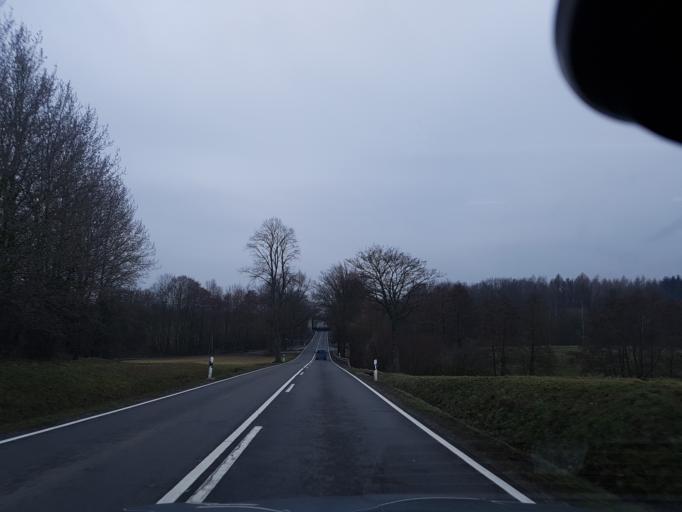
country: DE
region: Saxony
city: Hainichen
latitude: 50.9938
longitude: 13.1181
